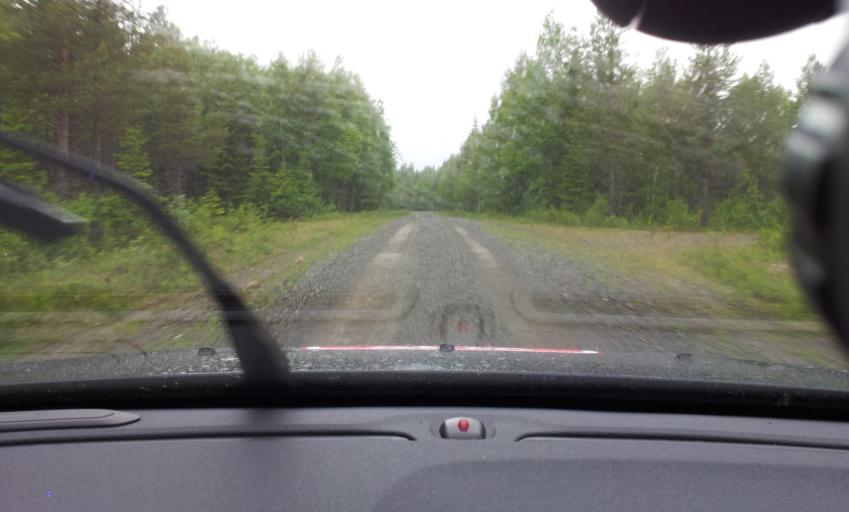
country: SE
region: Jaemtland
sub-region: Are Kommun
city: Are
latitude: 63.1902
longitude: 13.1763
